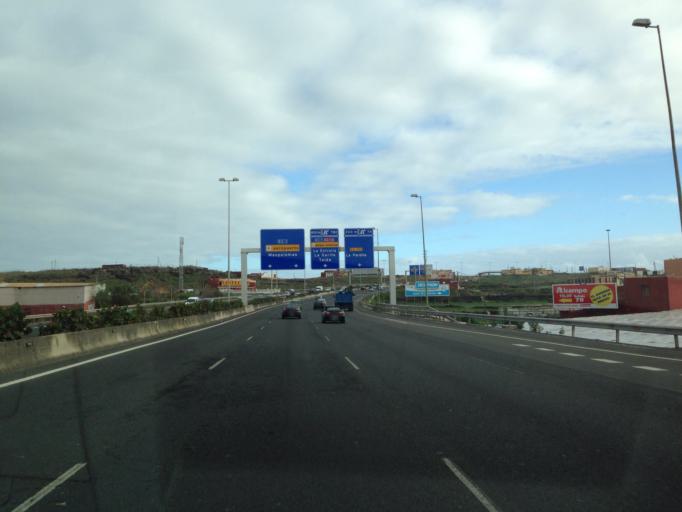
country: ES
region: Canary Islands
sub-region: Provincia de Las Palmas
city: Telde
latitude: 28.0238
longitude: -15.3902
